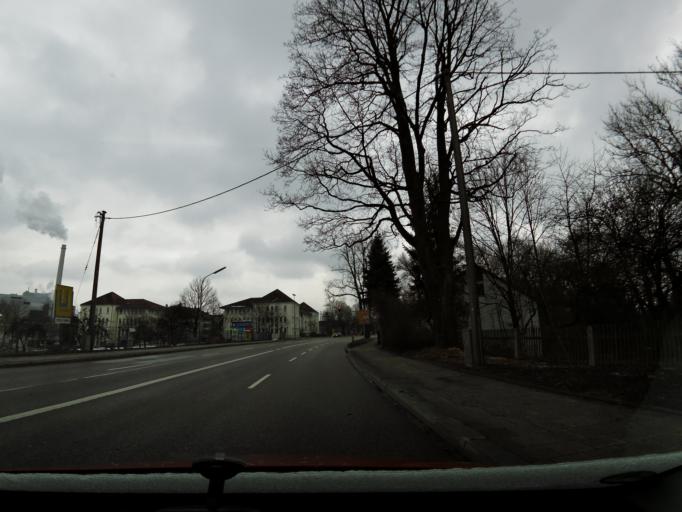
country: DE
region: Bavaria
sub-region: Upper Bavaria
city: Unterfoehring
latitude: 48.1851
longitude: 11.6340
